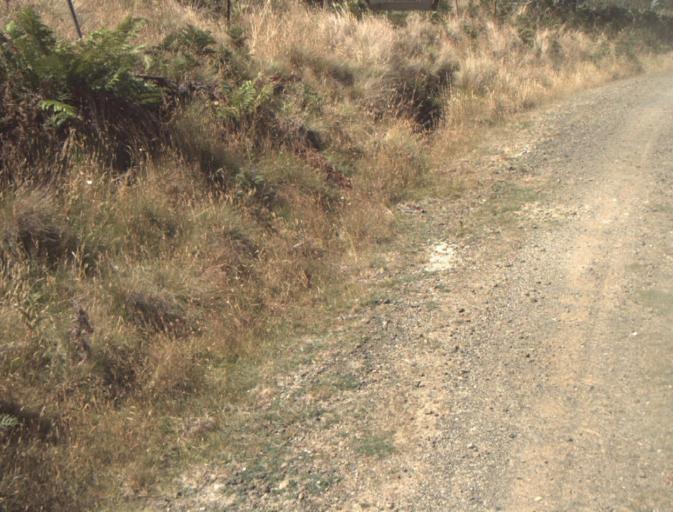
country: AU
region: Tasmania
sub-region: Dorset
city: Scottsdale
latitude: -41.3513
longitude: 147.4423
